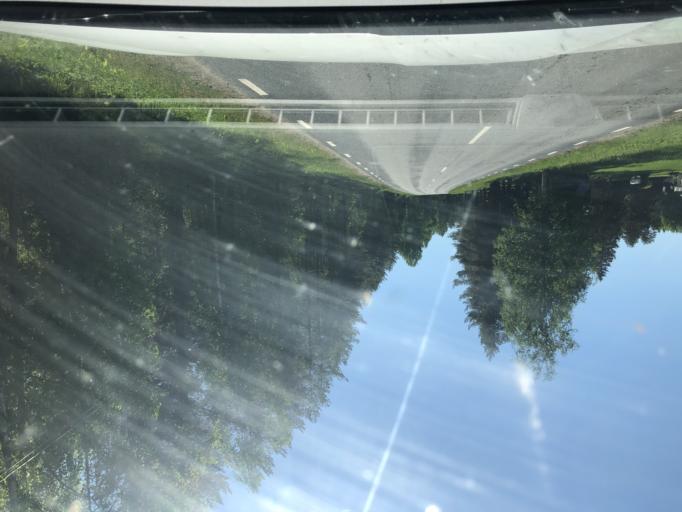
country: SE
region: Norrbotten
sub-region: Lulea Kommun
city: Sodra Sunderbyn
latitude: 65.6626
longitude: 21.9735
